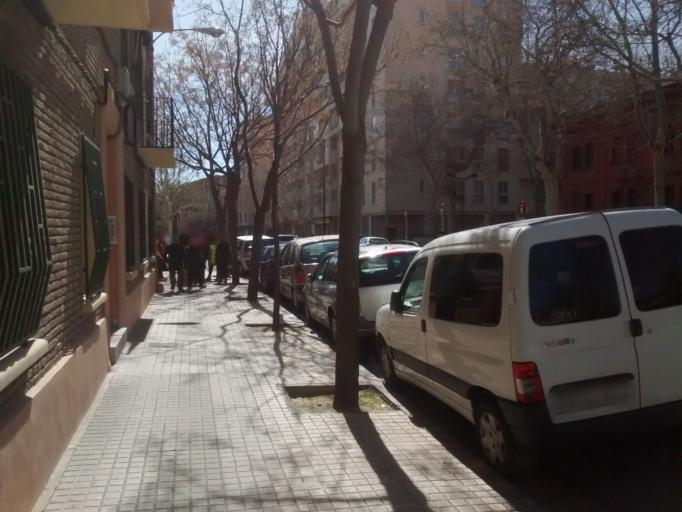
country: ES
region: Aragon
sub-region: Provincia de Zaragoza
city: Zaragoza
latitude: 41.6451
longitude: -0.8685
